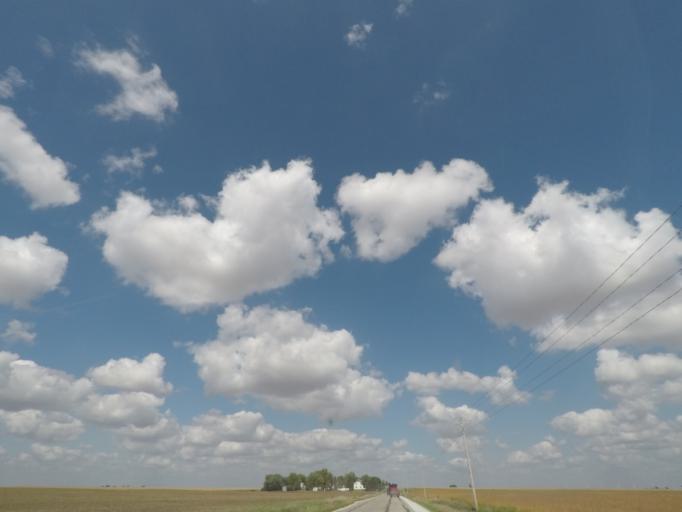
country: US
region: Iowa
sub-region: Story County
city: Nevada
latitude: 42.0665
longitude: -93.4056
